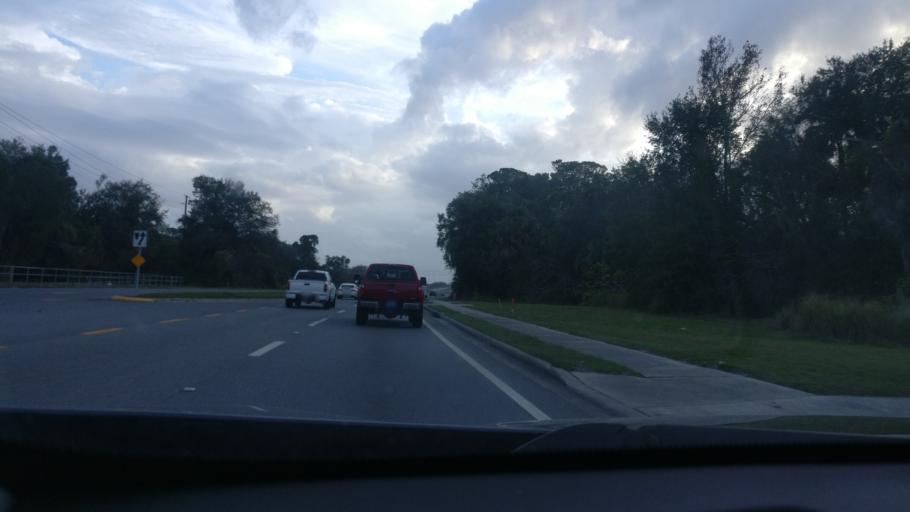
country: US
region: Florida
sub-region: Volusia County
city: DeBary
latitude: 28.8440
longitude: -81.3223
